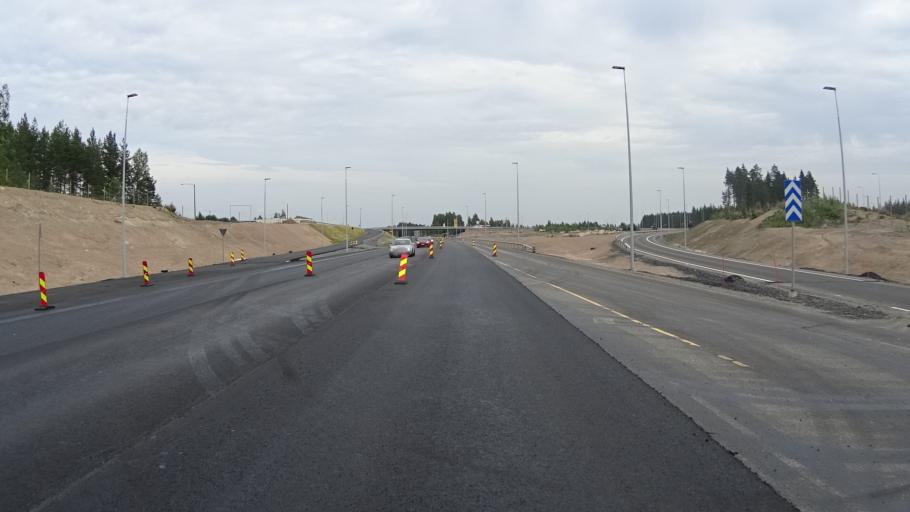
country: FI
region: South Karelia
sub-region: Lappeenranta
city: Luumaeki
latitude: 60.9285
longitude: 27.6236
